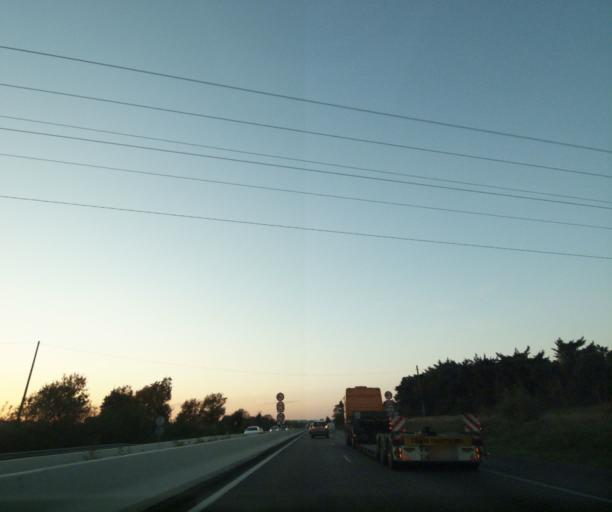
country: FR
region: Provence-Alpes-Cote d'Azur
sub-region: Departement des Bouches-du-Rhone
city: Arles
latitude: 43.6584
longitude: 4.6471
